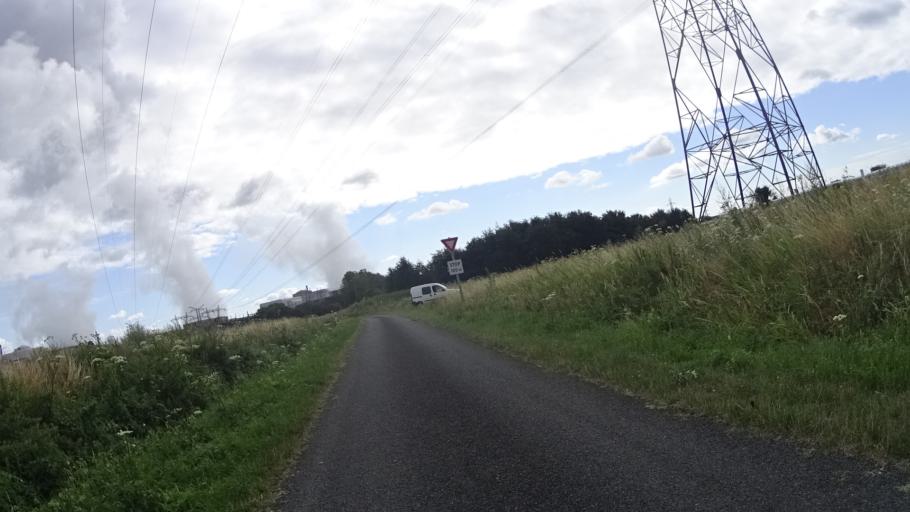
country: FR
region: Centre
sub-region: Departement d'Indre-et-Loire
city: Savigny-en-Veron
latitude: 47.2220
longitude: 0.1556
